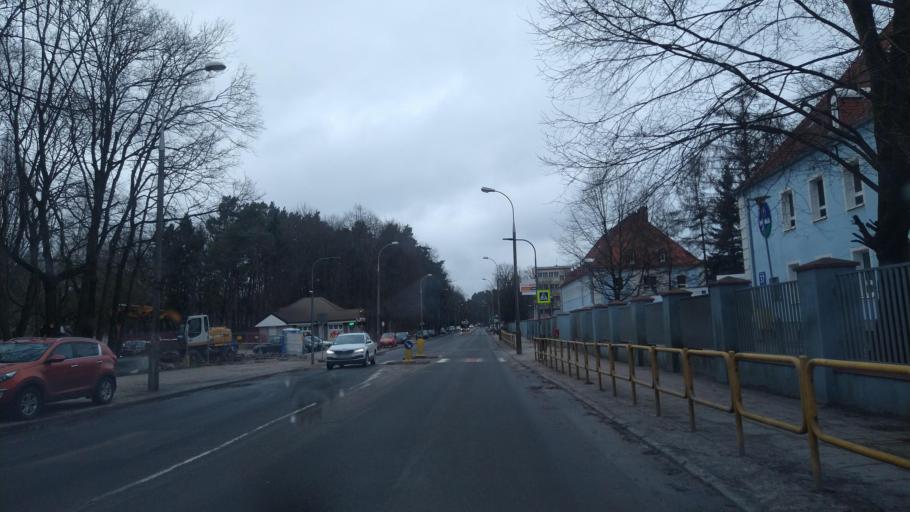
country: PL
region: Warmian-Masurian Voivodeship
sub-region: Powiat olsztynski
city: Olsztyn
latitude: 53.7933
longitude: 20.4824
